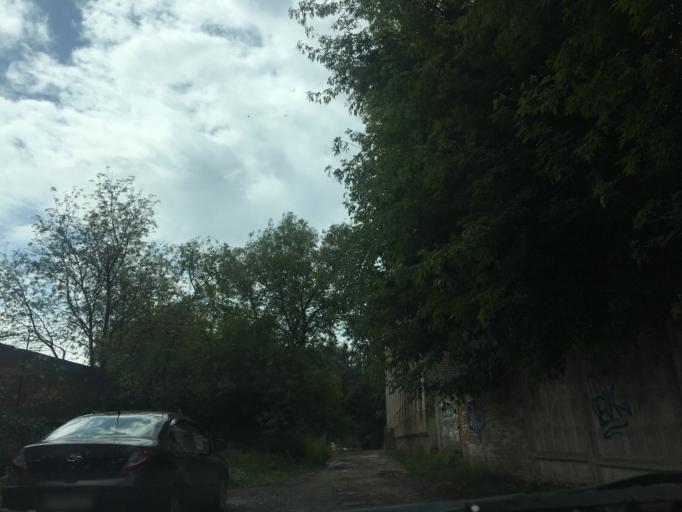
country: RU
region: Tula
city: Mendeleyevskiy
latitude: 54.1514
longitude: 37.5897
